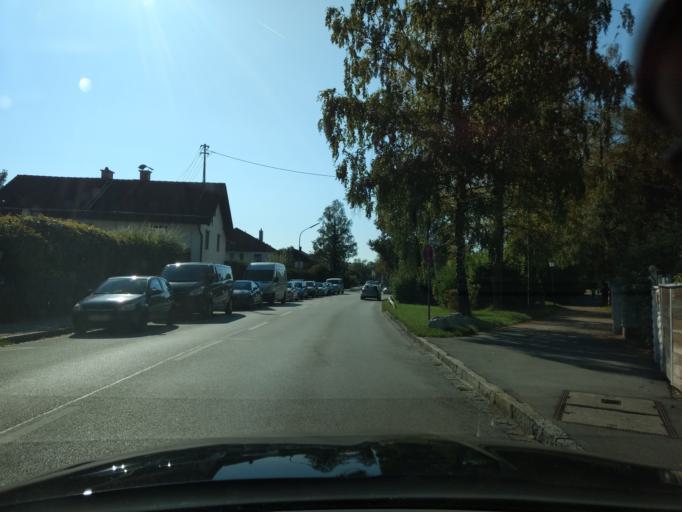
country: DE
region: Bavaria
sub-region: Upper Bavaria
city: Wolfratshausen
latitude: 47.9108
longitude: 11.4180
